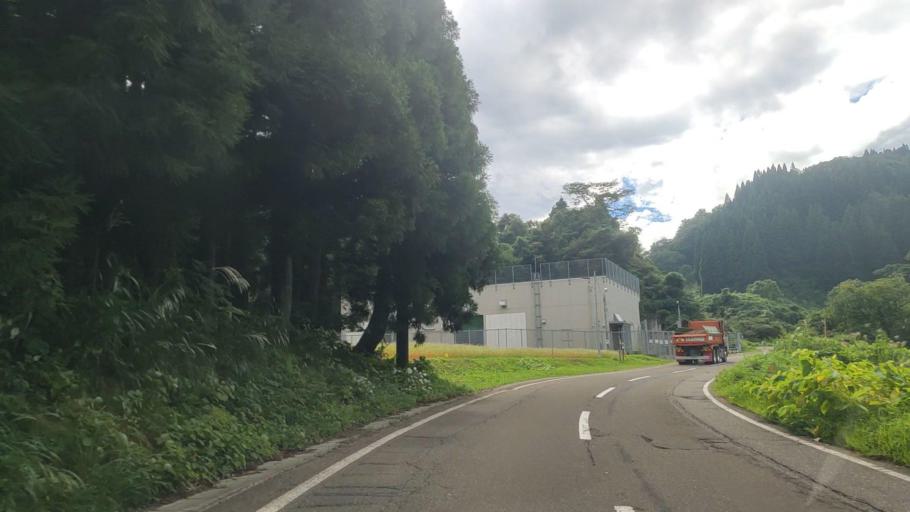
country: JP
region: Niigata
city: Arai
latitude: 36.9371
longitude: 138.2940
